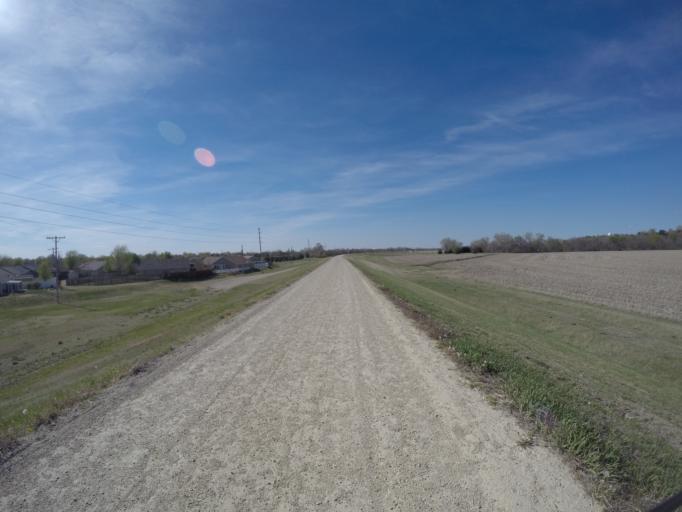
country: US
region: Kansas
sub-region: Saline County
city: Salina
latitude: 38.8207
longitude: -97.5847
